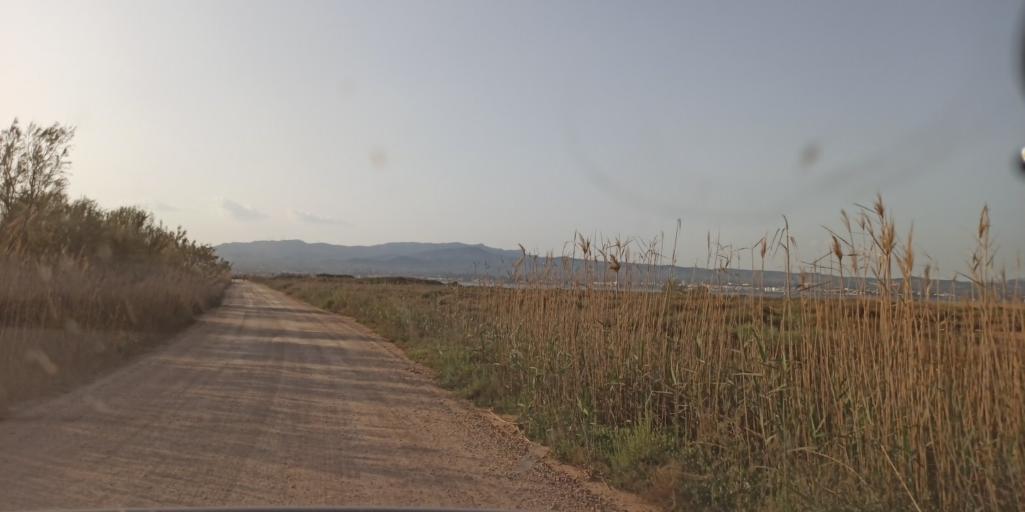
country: ES
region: Catalonia
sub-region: Provincia de Tarragona
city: L'Ampolla
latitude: 40.7771
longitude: 0.7225
